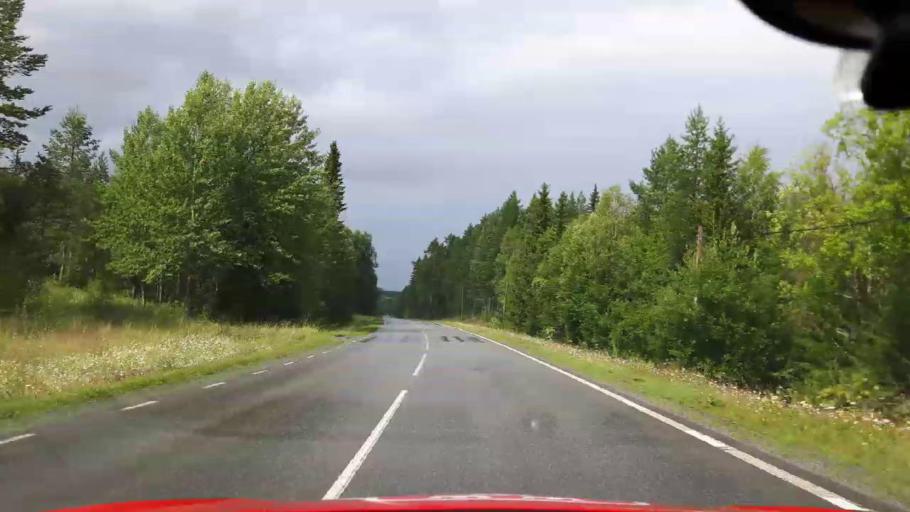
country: SE
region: Jaemtland
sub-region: Krokoms Kommun
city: Krokom
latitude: 63.3383
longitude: 14.2746
